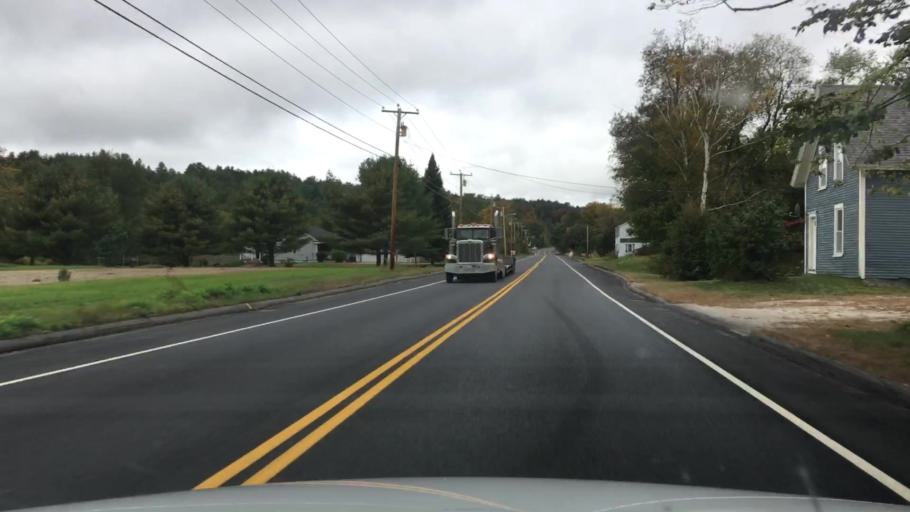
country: US
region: Maine
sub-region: Oxford County
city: Bethel
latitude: 44.4106
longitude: -70.8133
